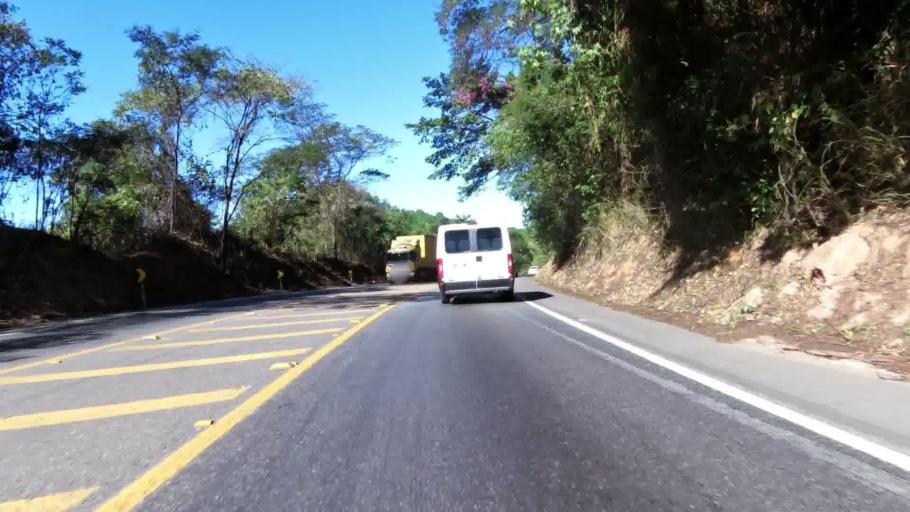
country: BR
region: Espirito Santo
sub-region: Alfredo Chaves
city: Alfredo Chaves
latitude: -20.7085
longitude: -40.7181
